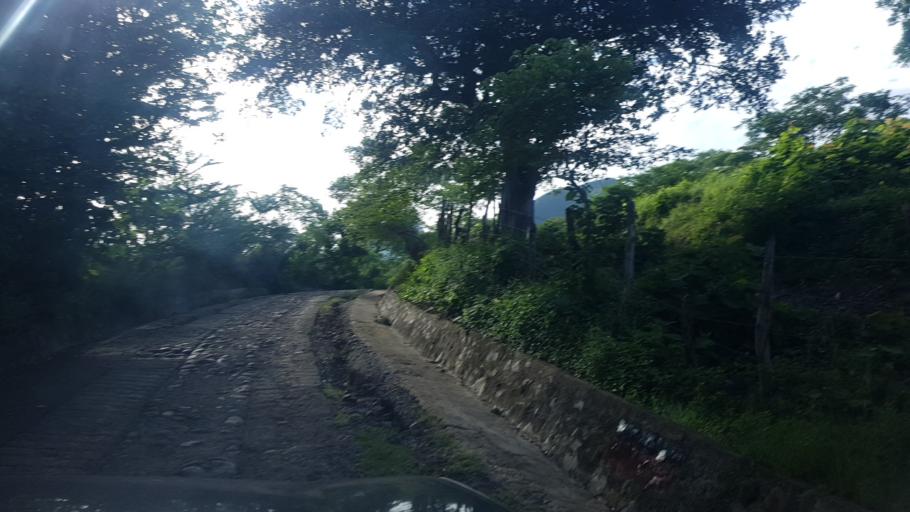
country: NI
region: Nueva Segovia
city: Ocotal
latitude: 13.6088
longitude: -86.4682
